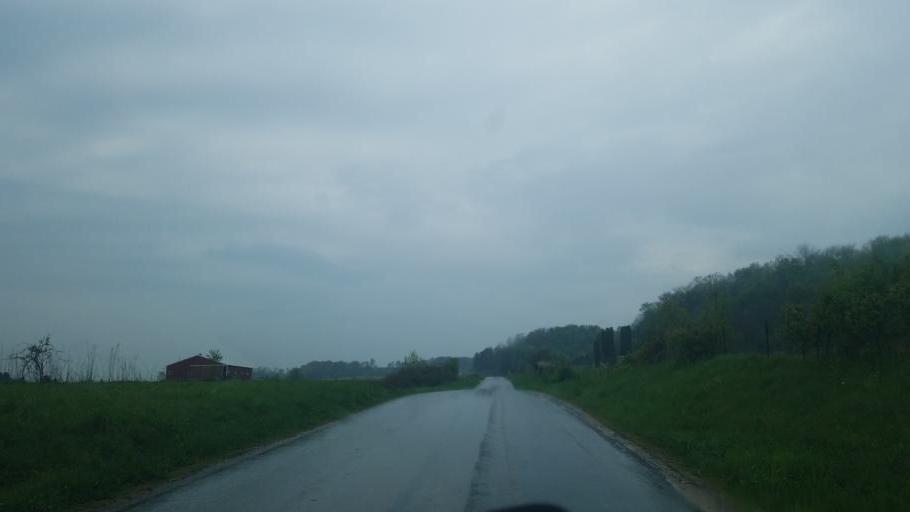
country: US
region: Wisconsin
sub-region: Vernon County
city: Hillsboro
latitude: 43.6188
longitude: -90.3876
